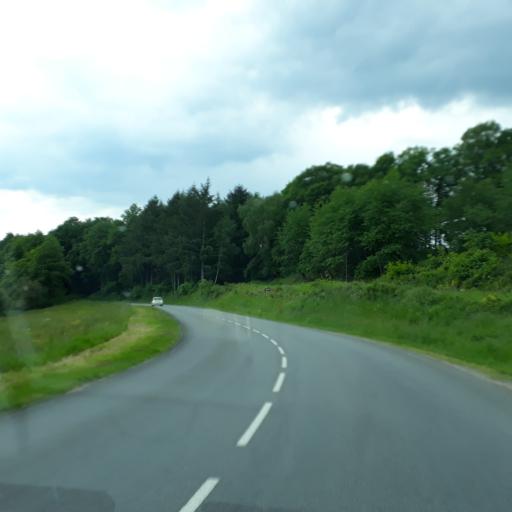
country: FR
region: Limousin
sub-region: Departement de la Haute-Vienne
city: Eymoutiers
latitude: 45.7605
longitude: 1.7465
